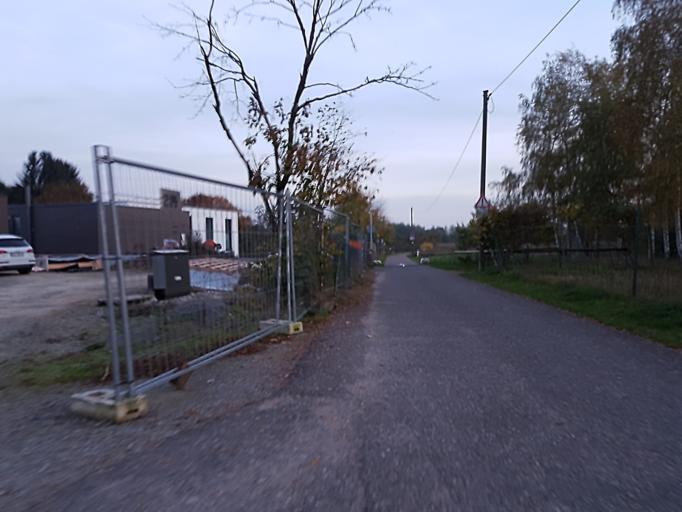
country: DE
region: Bavaria
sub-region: Regierungsbezirk Unterfranken
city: Niedernberg
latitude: 49.8989
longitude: 9.1434
